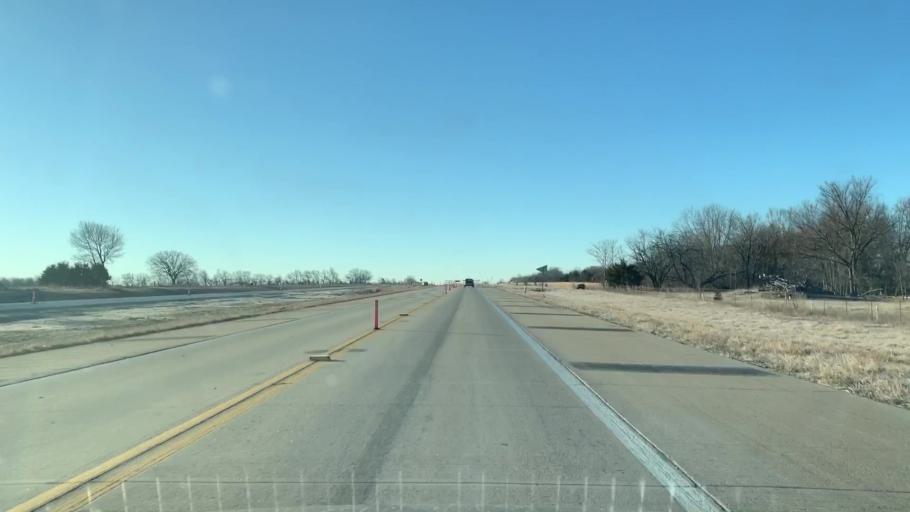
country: US
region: Kansas
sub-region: Bourbon County
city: Fort Scott
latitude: 37.7553
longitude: -94.7051
